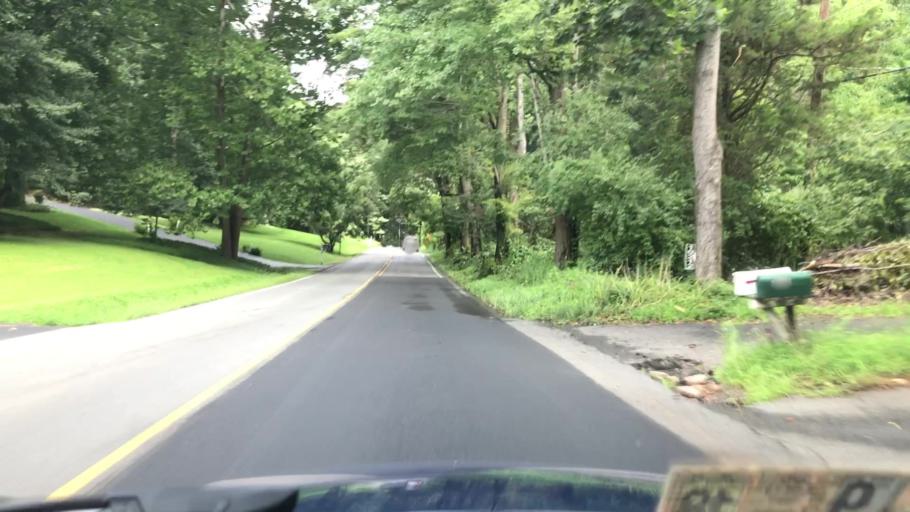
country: US
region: Virginia
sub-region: Fairfax County
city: Wolf Trap
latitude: 38.9157
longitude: -77.2981
